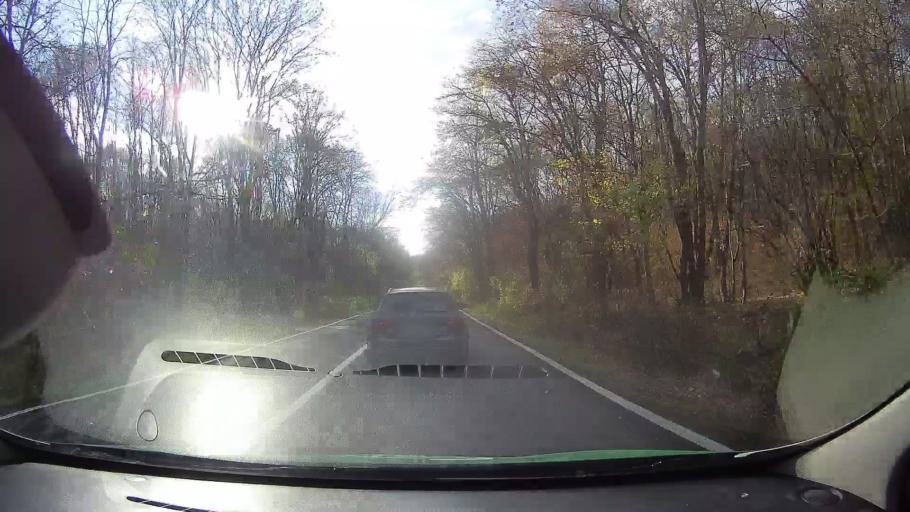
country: RO
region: Tulcea
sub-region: Comuna Ciucurova
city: Ciucurova
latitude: 44.9235
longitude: 28.4325
